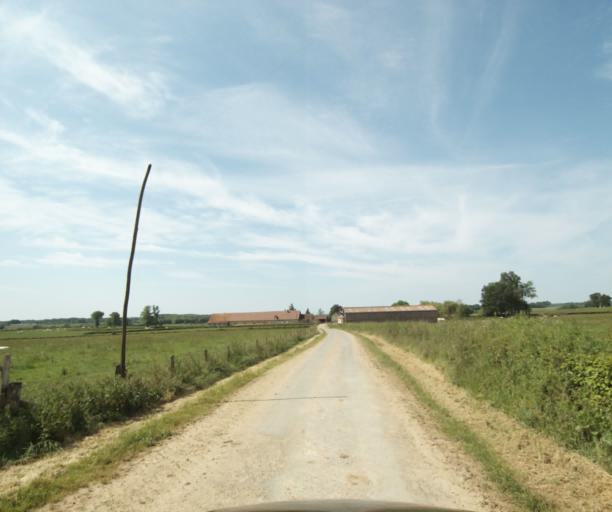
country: FR
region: Bourgogne
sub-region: Departement de Saone-et-Loire
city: Palinges
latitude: 46.5614
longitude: 4.1697
